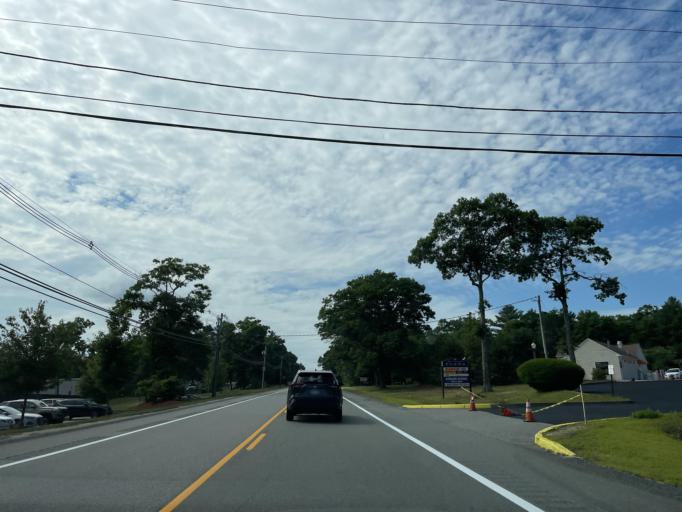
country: US
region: Rhode Island
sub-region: Kent County
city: West Greenwich
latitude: 41.6117
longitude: -71.6658
